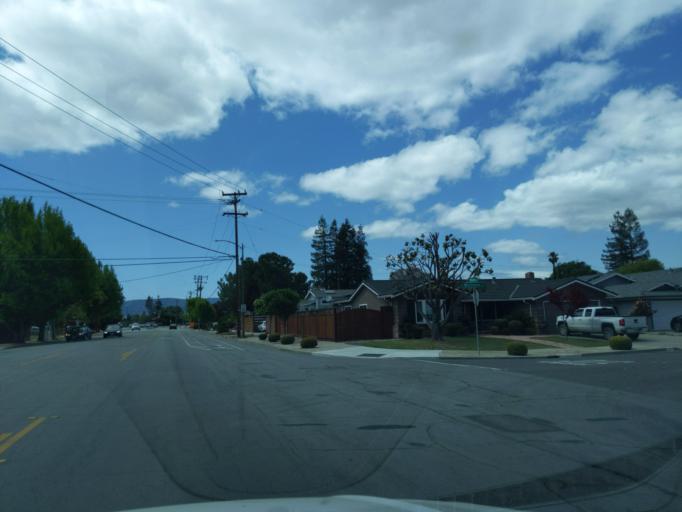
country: US
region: California
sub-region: Santa Clara County
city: Campbell
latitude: 37.3088
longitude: -121.9604
